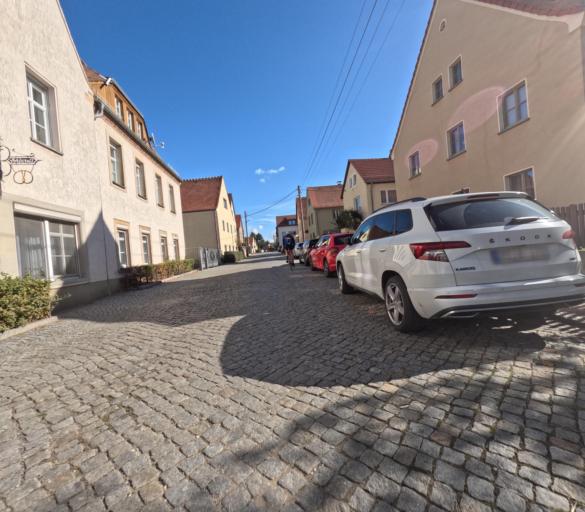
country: DE
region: Saxony
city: Radebeul
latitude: 51.1191
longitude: 13.6689
